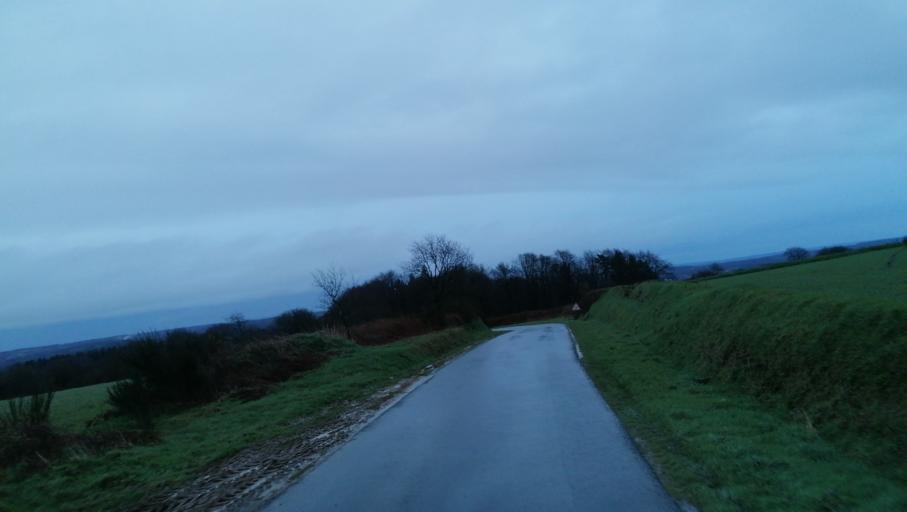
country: FR
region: Brittany
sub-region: Departement des Cotes-d'Armor
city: Plouagat
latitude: 48.4868
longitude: -2.9906
